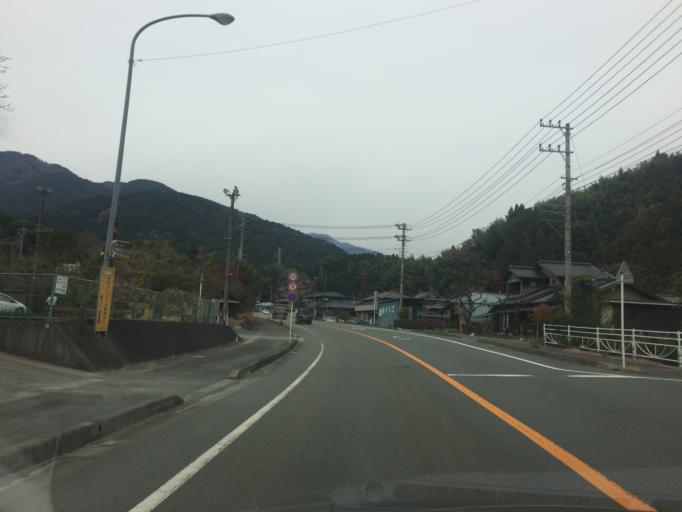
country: JP
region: Shizuoka
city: Fujinomiya
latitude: 35.2633
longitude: 138.4656
